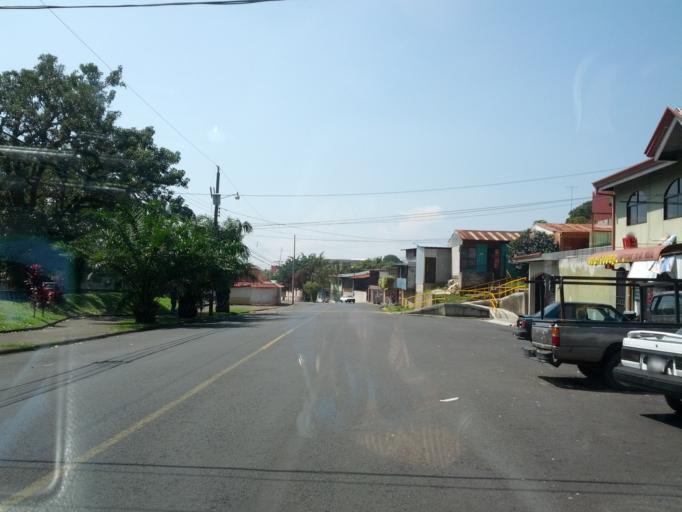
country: CR
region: Alajuela
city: Alajuela
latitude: 10.0161
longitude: -84.2016
